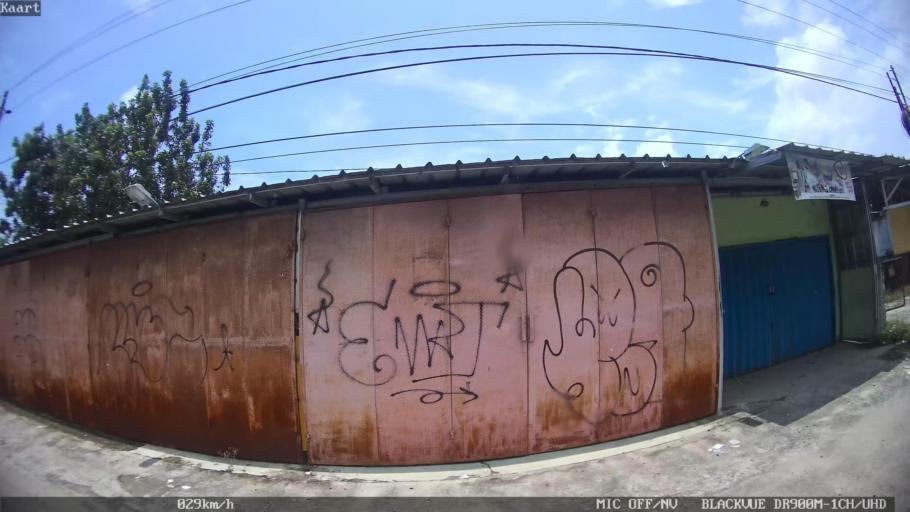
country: ID
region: Lampung
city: Kedaton
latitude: -5.3854
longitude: 105.2562
